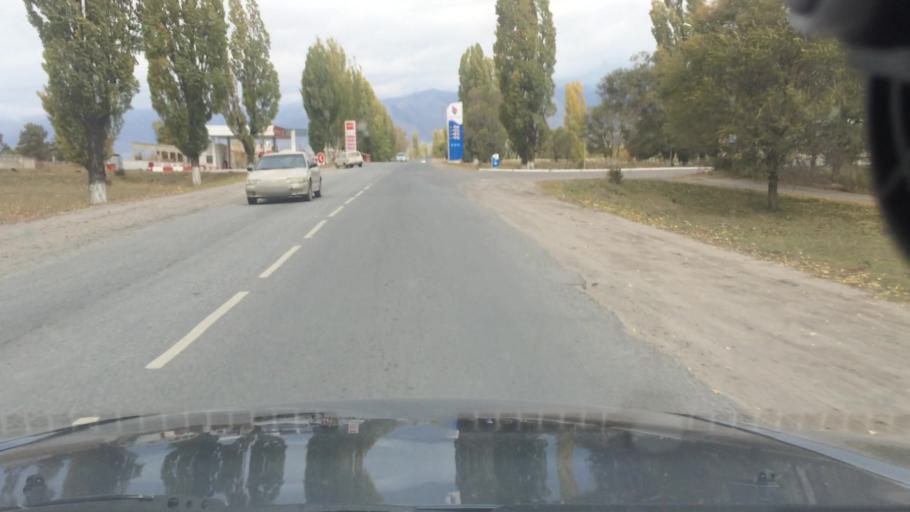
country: KG
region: Ysyk-Koel
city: Tyup
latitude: 42.7393
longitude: 78.3449
